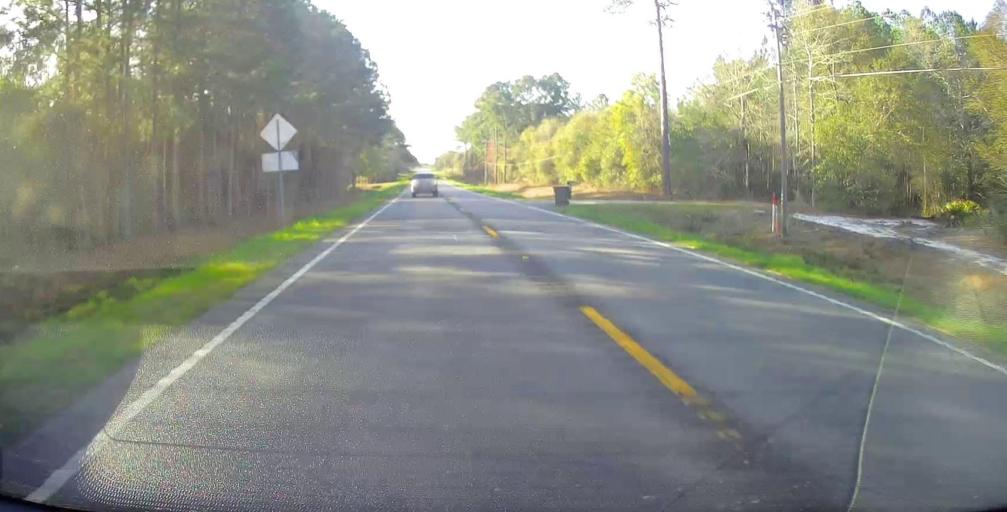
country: US
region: Georgia
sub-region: Tattnall County
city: Reidsville
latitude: 32.1065
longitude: -82.1719
